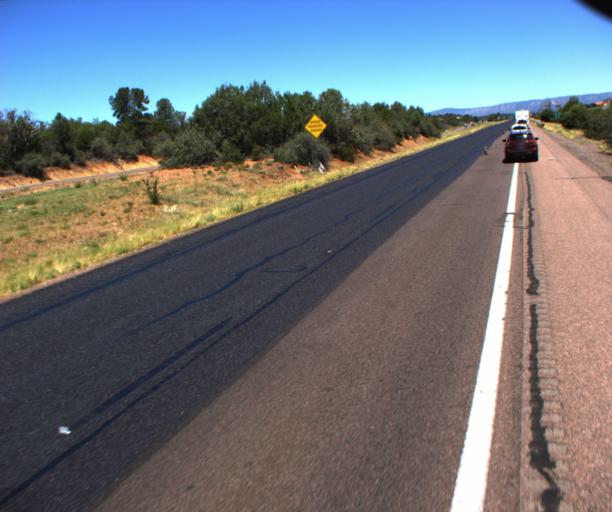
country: US
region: Arizona
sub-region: Gila County
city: Payson
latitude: 34.2131
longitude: -111.3316
